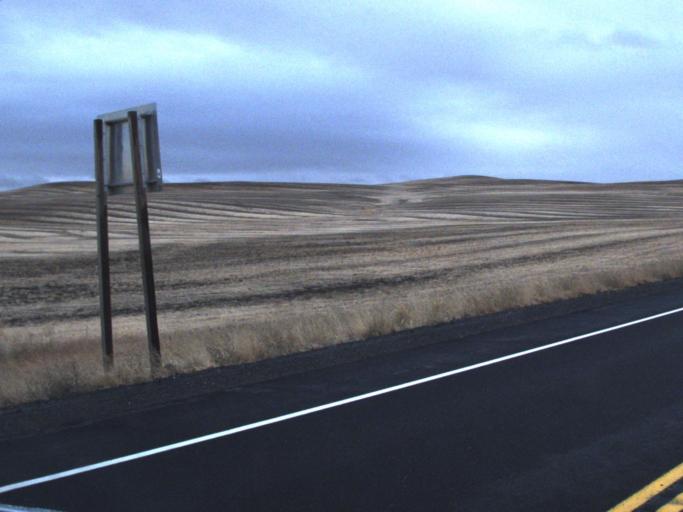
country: US
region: Washington
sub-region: Spokane County
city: Cheney
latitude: 47.4199
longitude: -117.3910
